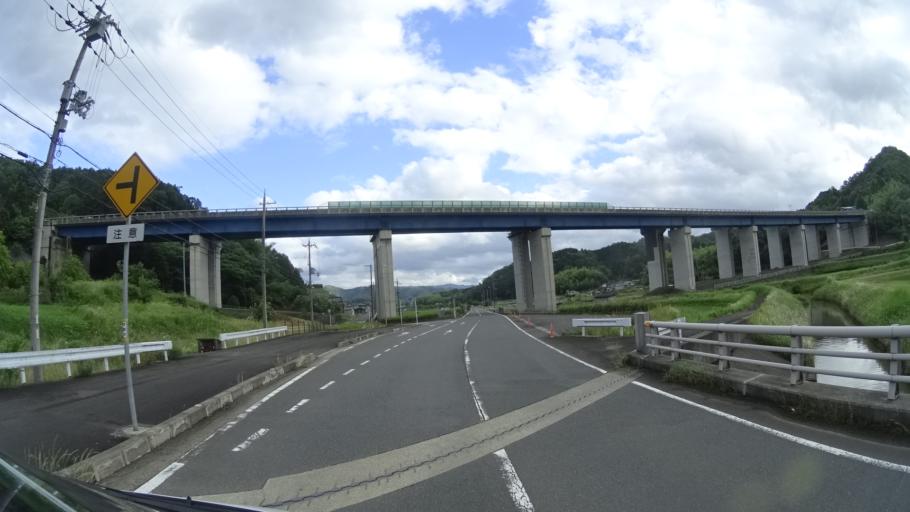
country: JP
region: Kyoto
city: Ayabe
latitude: 35.3484
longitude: 135.2881
